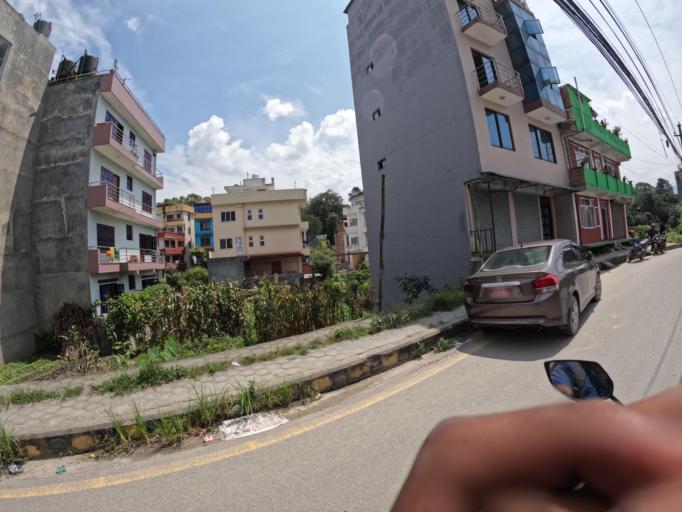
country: NP
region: Central Region
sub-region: Bagmati Zone
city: Bhaktapur
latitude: 27.6763
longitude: 85.3823
